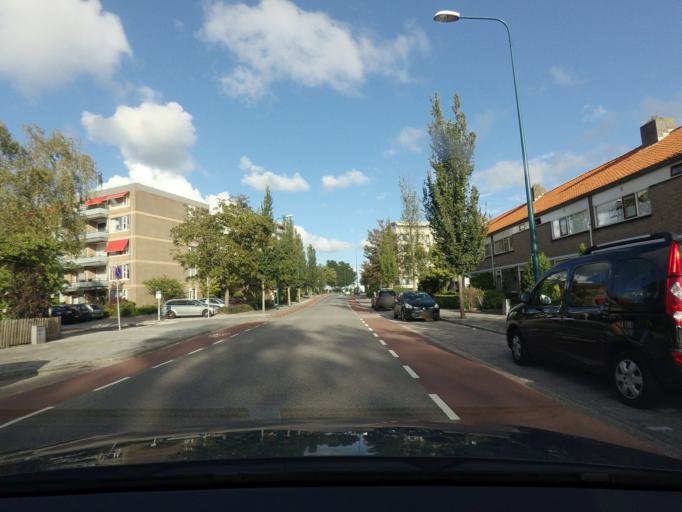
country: NL
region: South Holland
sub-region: Gemeente Oegstgeest
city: Oegstgeest
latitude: 52.1906
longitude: 4.4711
